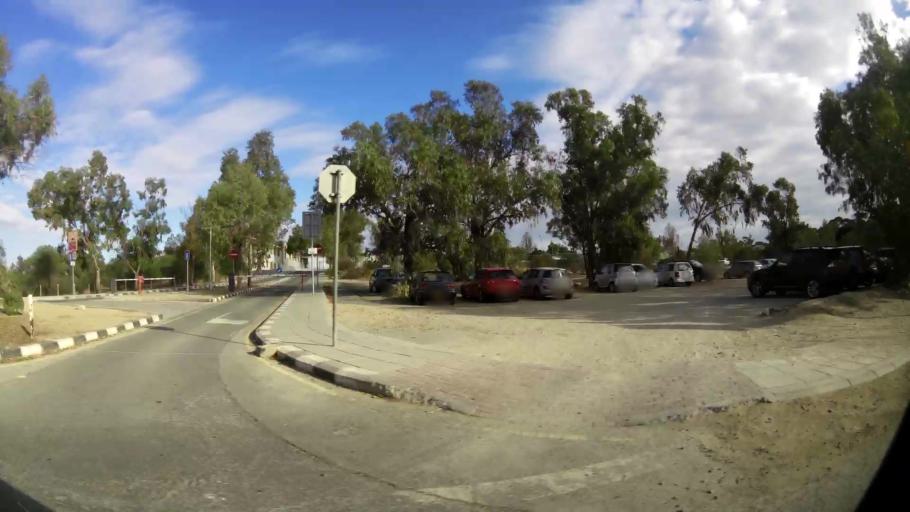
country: CY
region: Lefkosia
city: Nicosia
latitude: 35.1493
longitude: 33.3505
